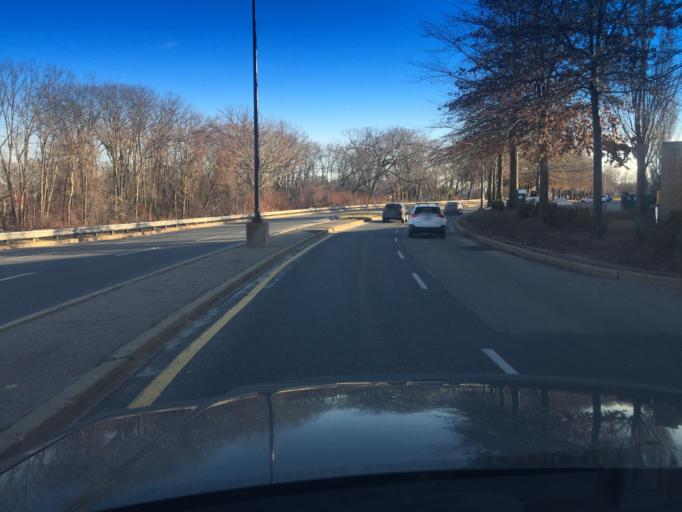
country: US
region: Massachusetts
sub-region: Middlesex County
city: Framingham
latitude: 42.3030
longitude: -71.3932
